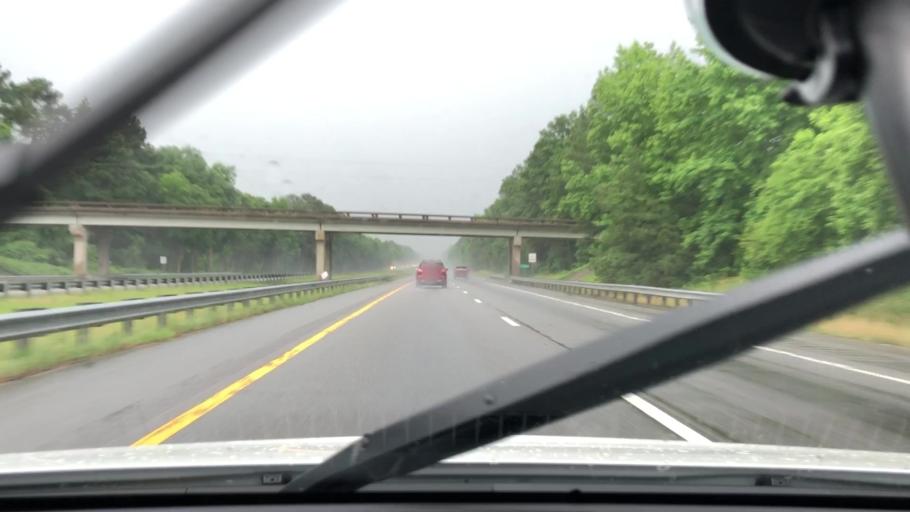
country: US
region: North Carolina
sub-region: Halifax County
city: Halifax
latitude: 36.3330
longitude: -77.6981
